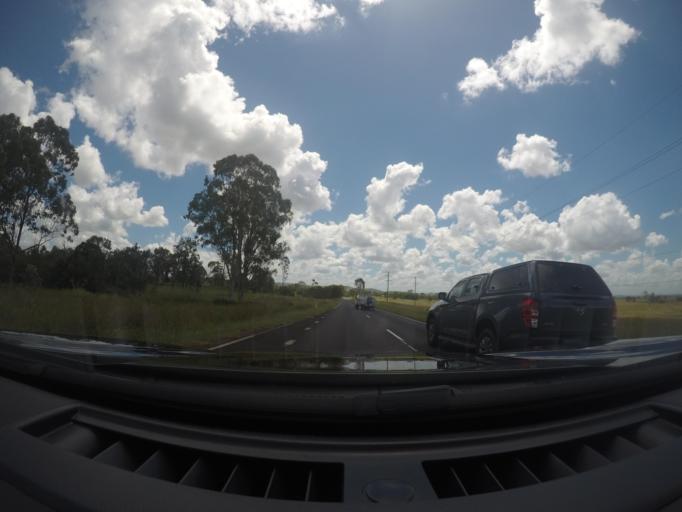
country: AU
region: Queensland
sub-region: Moreton Bay
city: Woodford
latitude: -27.1428
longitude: 152.4906
